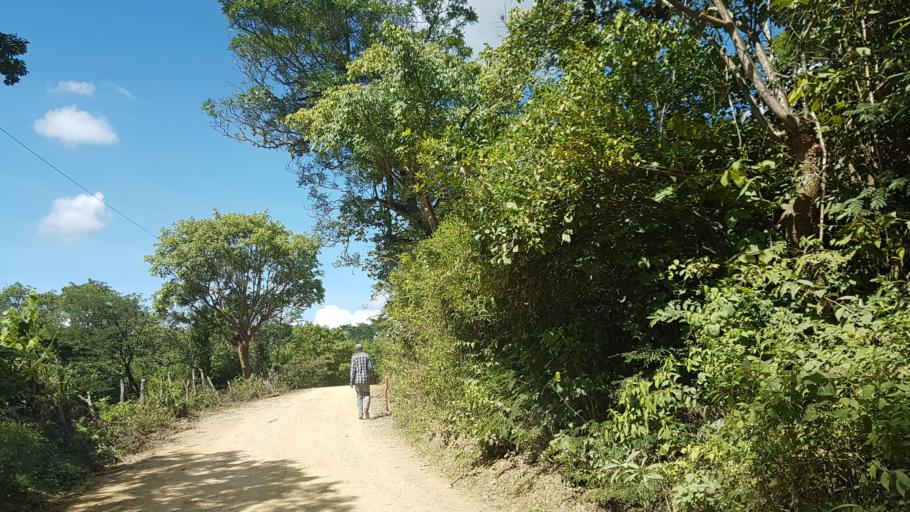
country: HN
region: El Paraiso
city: Santa Cruz
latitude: 13.7353
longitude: -86.6960
